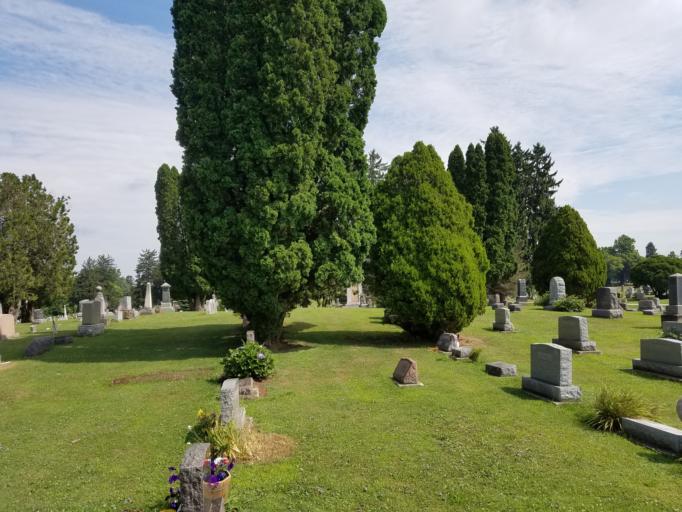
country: US
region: Ohio
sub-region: Knox County
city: Fredericktown
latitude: 40.4749
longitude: -82.6779
